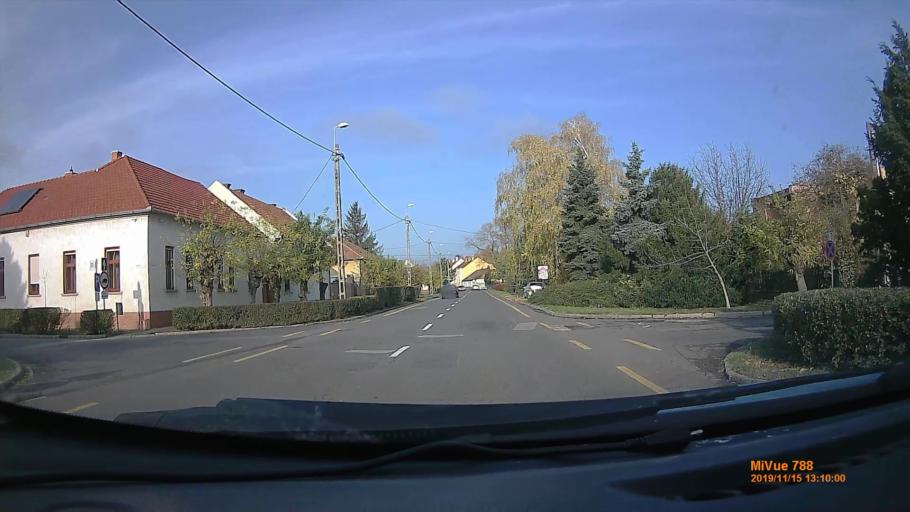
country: HU
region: Bekes
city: Gyula
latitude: 46.6416
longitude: 21.2794
